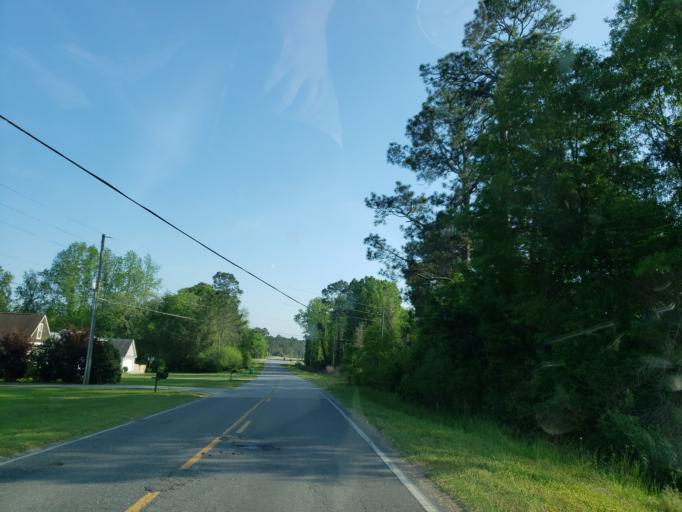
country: US
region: Georgia
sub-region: Tift County
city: Tifton
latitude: 31.4843
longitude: -83.5433
